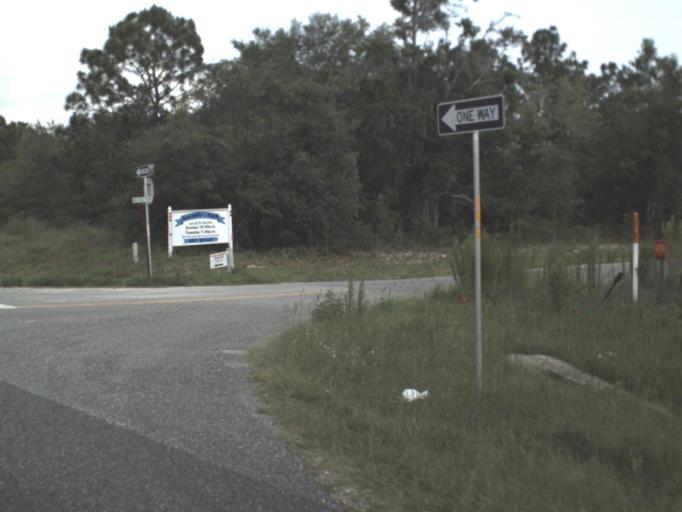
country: US
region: Florida
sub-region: Levy County
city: East Bronson
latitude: 29.4246
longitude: -82.5858
